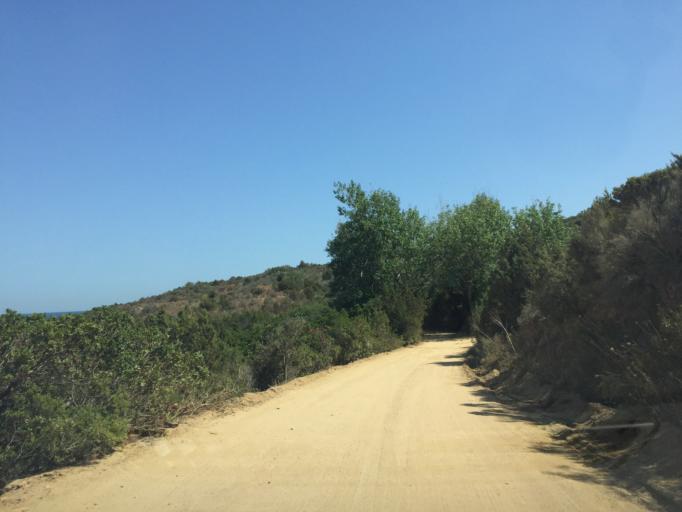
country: IT
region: Sardinia
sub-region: Provincia di Olbia-Tempio
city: San Teodoro
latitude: 40.8402
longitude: 9.7182
